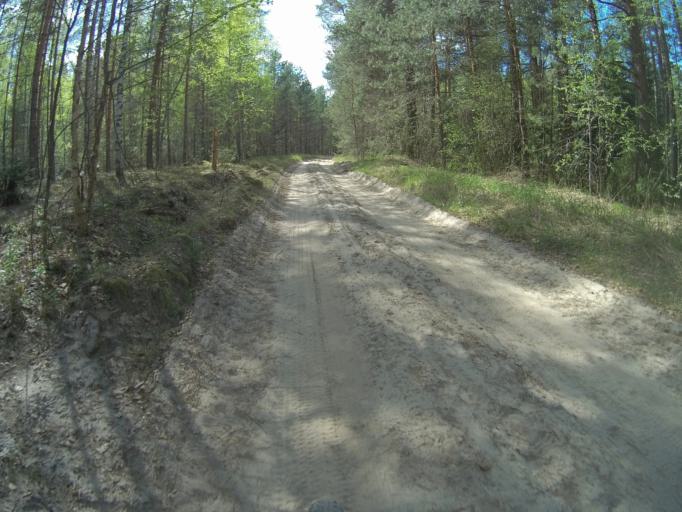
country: RU
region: Vladimir
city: Vorsha
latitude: 55.9632
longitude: 40.1933
